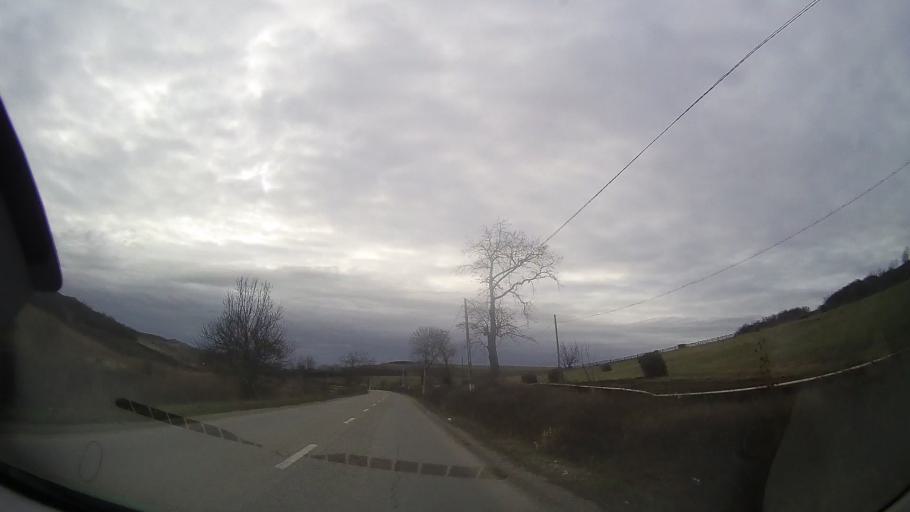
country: RO
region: Bistrita-Nasaud
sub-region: Comuna Budesti
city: Budesti
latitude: 46.8625
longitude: 24.2441
